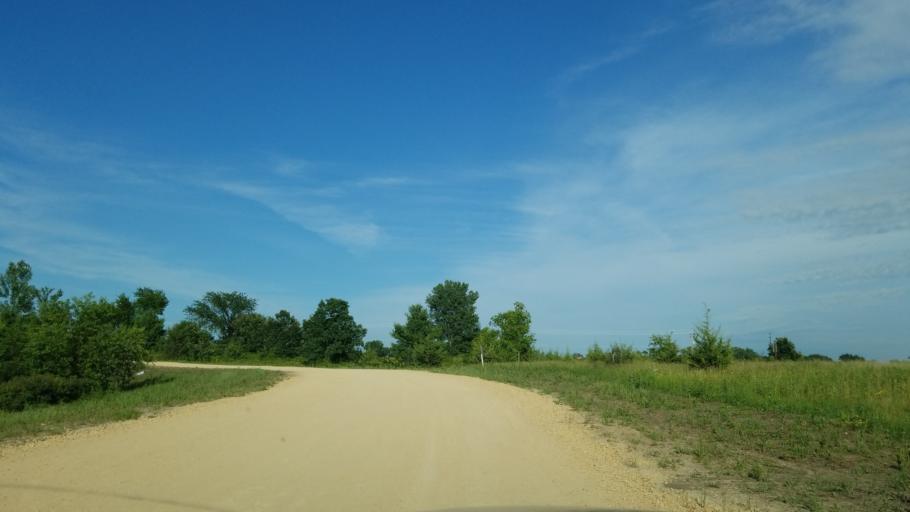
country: US
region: Wisconsin
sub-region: Saint Croix County
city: North Hudson
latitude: 45.0129
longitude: -92.6776
